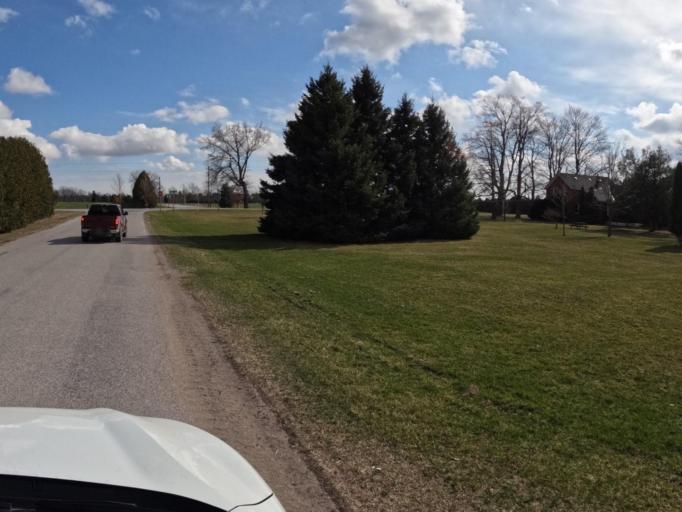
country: CA
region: Ontario
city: Norfolk County
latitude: 42.9005
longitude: -80.2890
